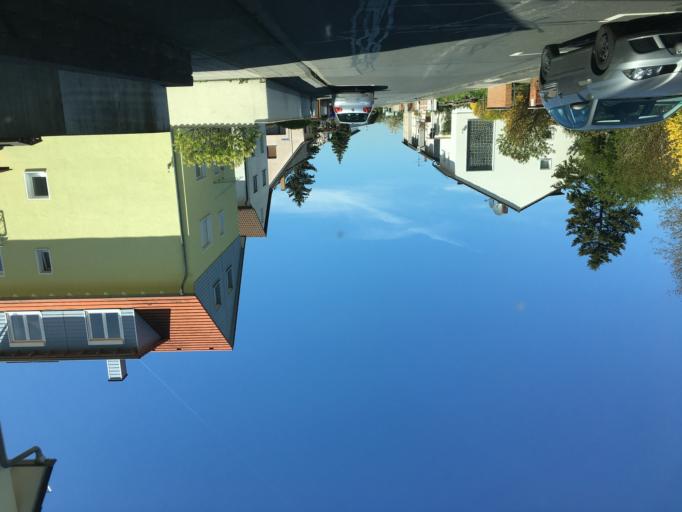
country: DE
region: Hesse
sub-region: Regierungsbezirk Darmstadt
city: Gross-Zimmern
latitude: 49.8797
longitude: 8.8174
